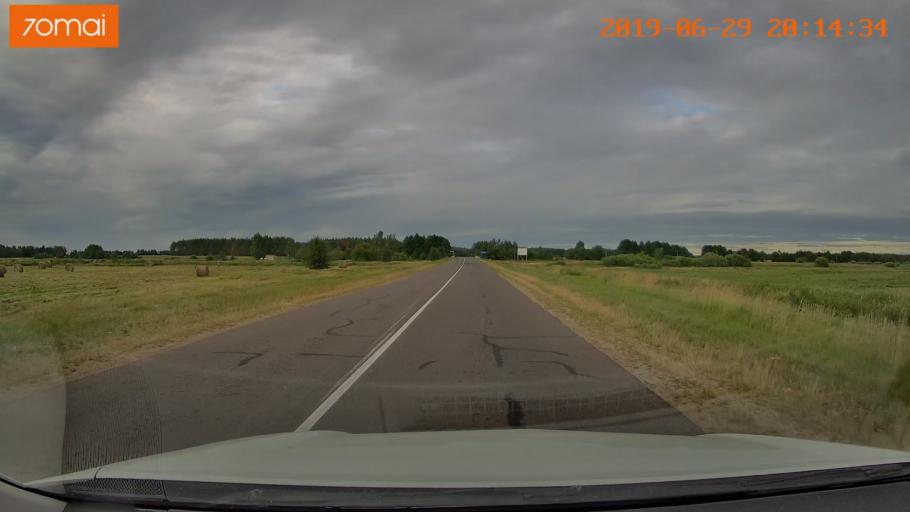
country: BY
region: Brest
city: Lahishyn
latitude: 52.3677
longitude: 26.1600
